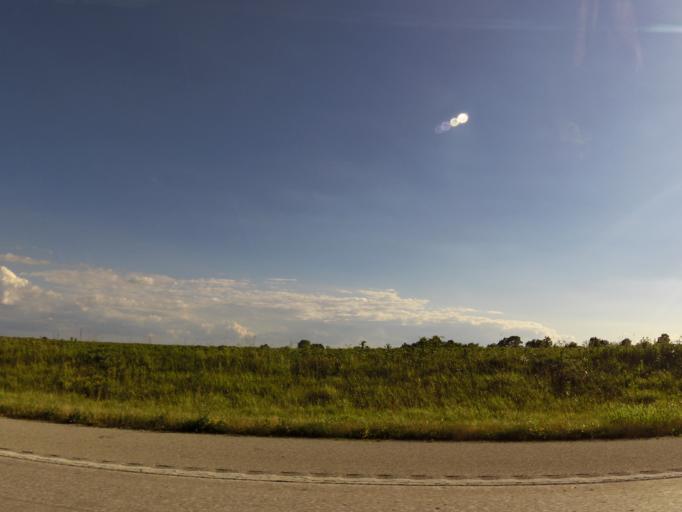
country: US
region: Missouri
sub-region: Pike County
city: Bowling Green
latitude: 39.2678
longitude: -91.0808
